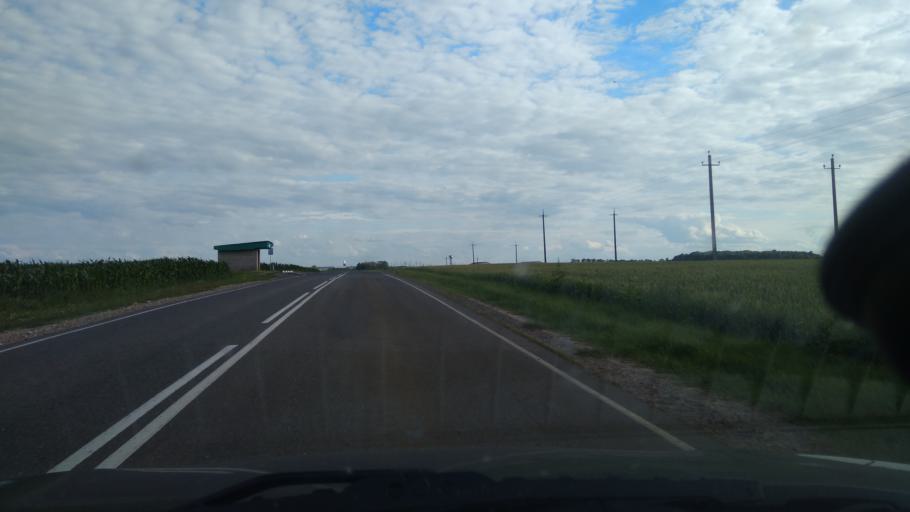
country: BY
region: Grodnenskaya
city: Zel'va
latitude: 53.2901
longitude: 24.6856
